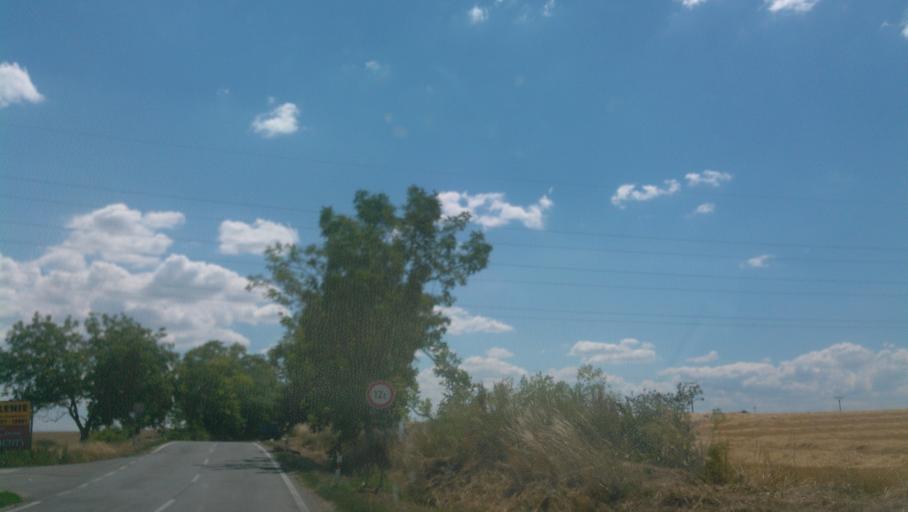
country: SK
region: Trnavsky
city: Vrbove
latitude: 48.5892
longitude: 17.7470
